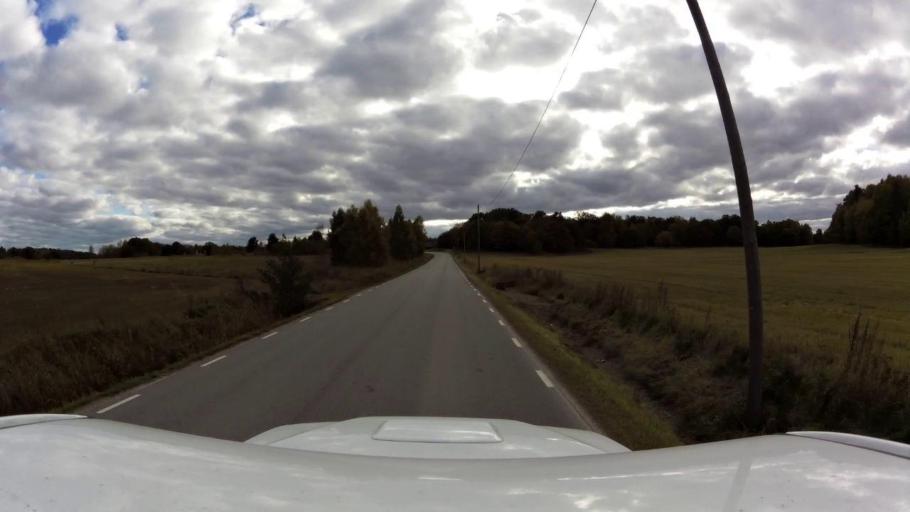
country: SE
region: OEstergoetland
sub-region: Linkopings Kommun
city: Linkoping
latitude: 58.3836
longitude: 15.5921
